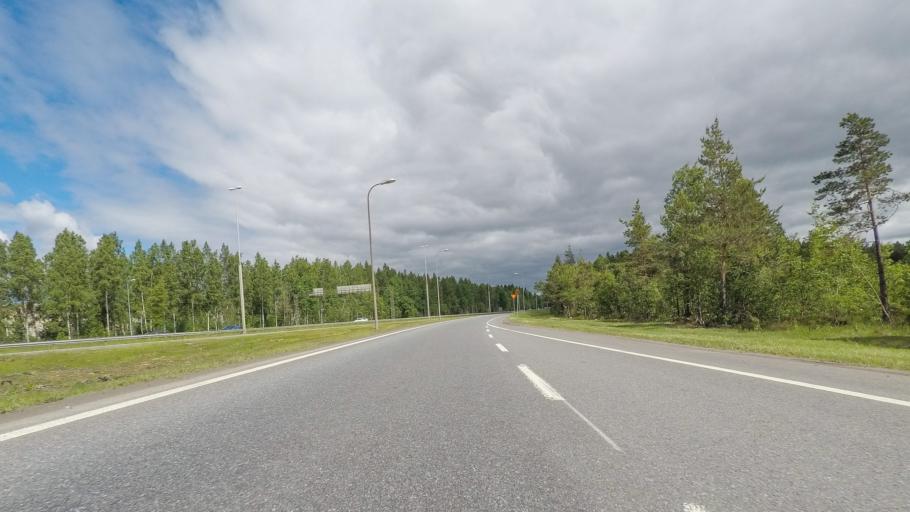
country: FI
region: Uusimaa
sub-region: Helsinki
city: Vantaa
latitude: 60.2388
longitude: 25.0463
